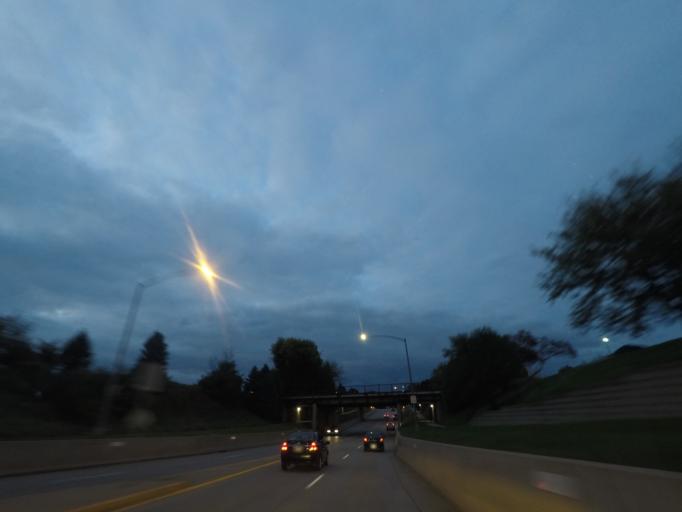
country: US
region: Iowa
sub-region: Story County
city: Ames
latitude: 42.0238
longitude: -93.6202
